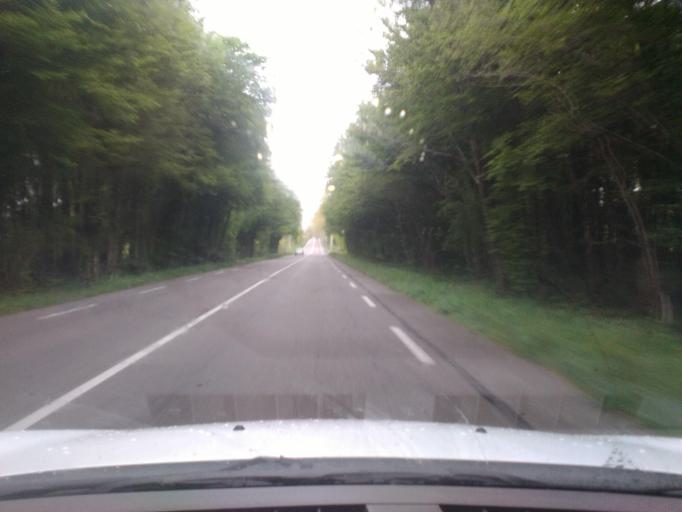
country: FR
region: Rhone-Alpes
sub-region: Departement de l'Ain
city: Servas
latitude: 46.1466
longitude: 5.1758
